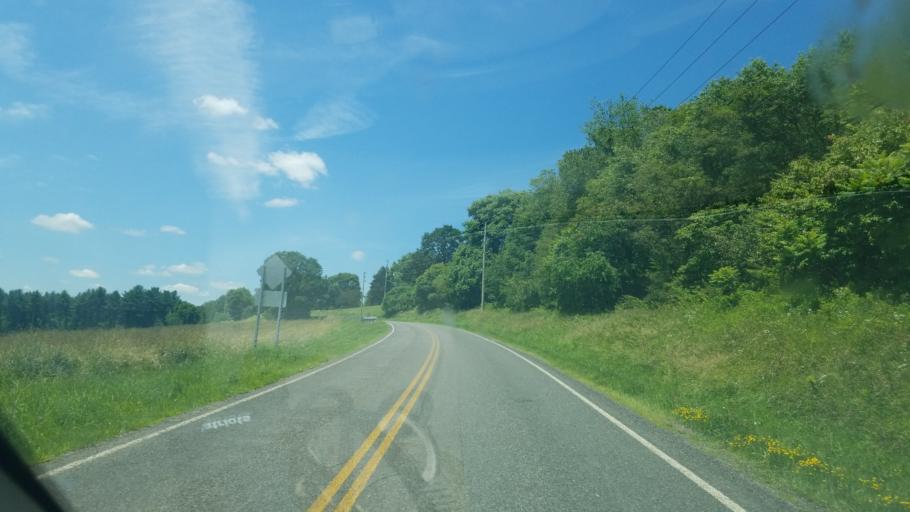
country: US
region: Ohio
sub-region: Columbiana County
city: Glenmoor
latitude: 40.7480
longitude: -80.6490
